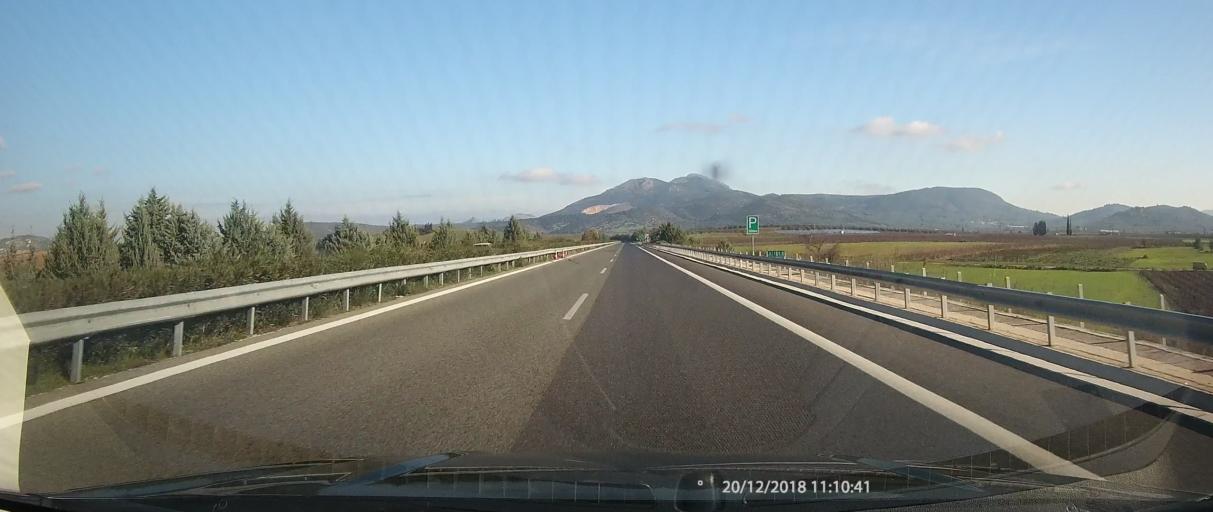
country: GR
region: Peloponnese
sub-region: Nomos Korinthias
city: Ayios Vasilios
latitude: 37.8219
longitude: 22.7929
